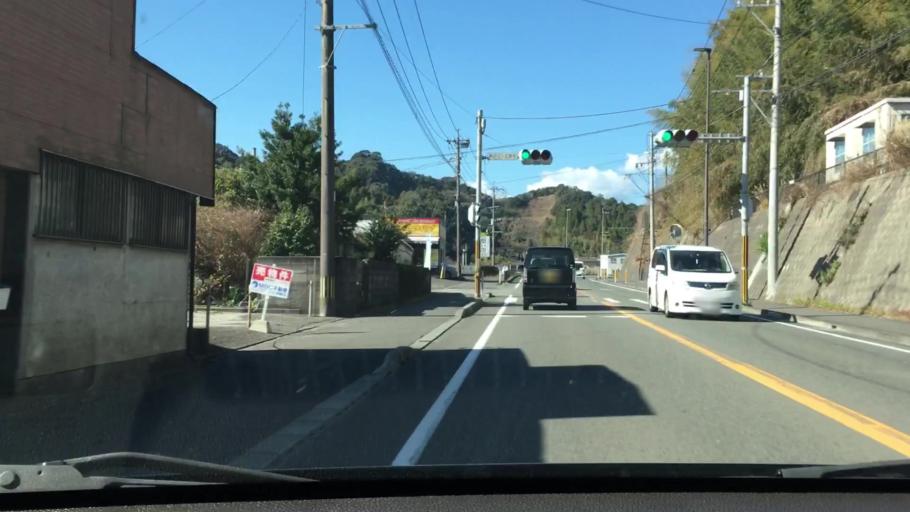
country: JP
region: Kagoshima
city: Kagoshima-shi
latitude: 31.6346
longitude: 130.5219
